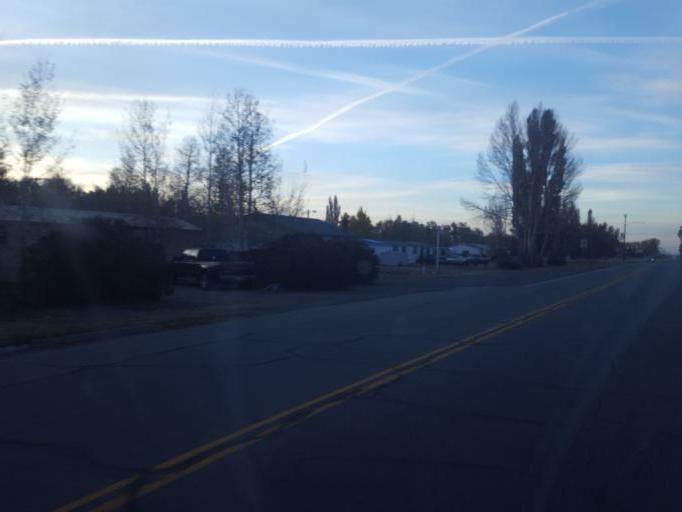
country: US
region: Colorado
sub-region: Rio Grande County
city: Monte Vista
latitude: 37.5761
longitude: -106.1496
